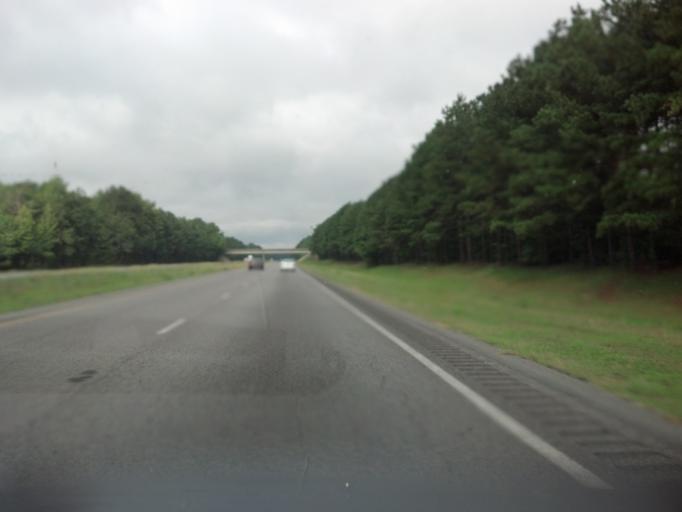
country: US
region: North Carolina
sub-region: Nash County
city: Rocky Mount
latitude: 35.9354
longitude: -77.7250
